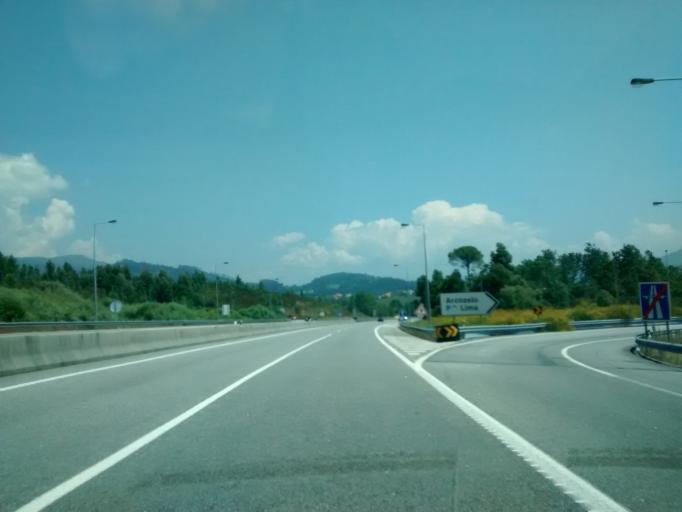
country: PT
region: Viana do Castelo
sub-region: Ponte de Lima
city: Ponte de Lima
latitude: 41.7862
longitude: -8.6009
